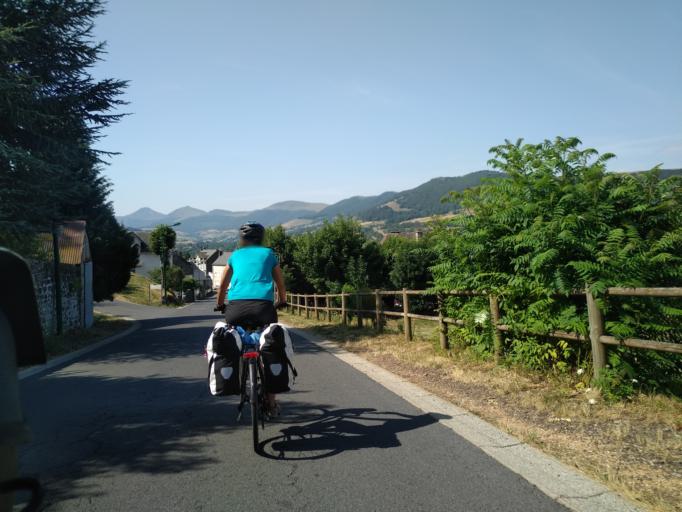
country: FR
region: Auvergne
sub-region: Departement du Cantal
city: Riom-es-Montagnes
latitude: 45.2116
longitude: 2.7177
